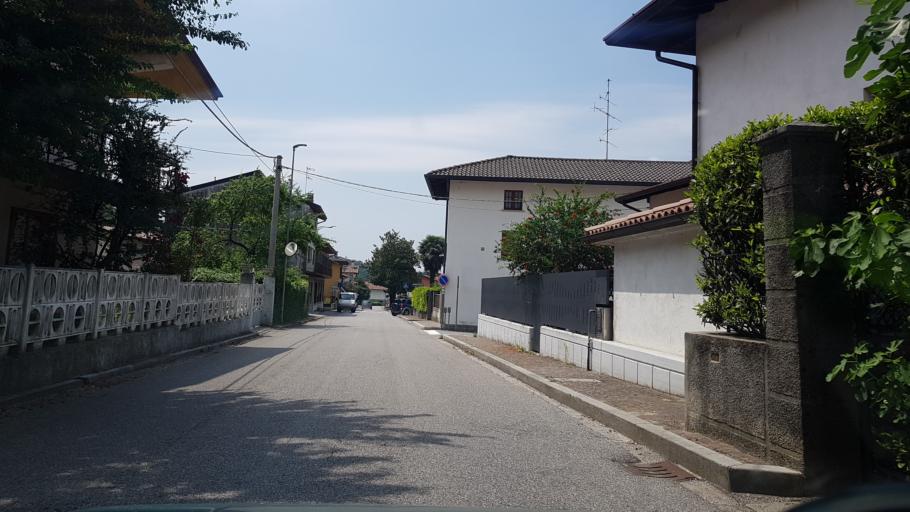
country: IT
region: Friuli Venezia Giulia
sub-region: Provincia di Udine
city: Torreano
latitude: 46.1307
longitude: 13.4329
